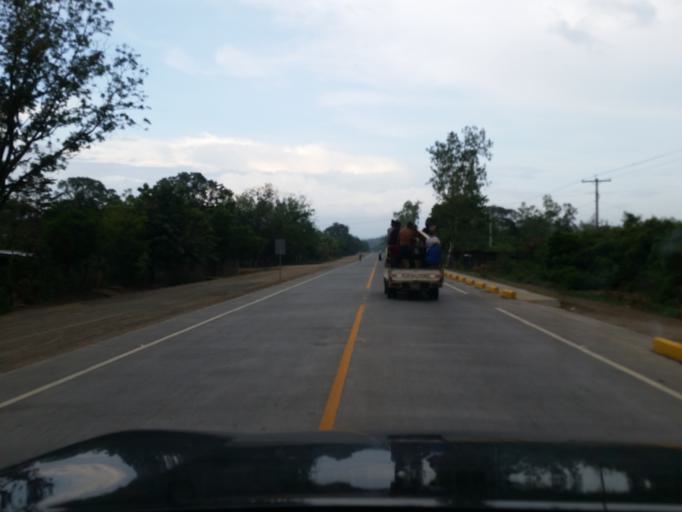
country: NI
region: Managua
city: Carlos Fonseca Amador
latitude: 12.0668
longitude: -86.4777
